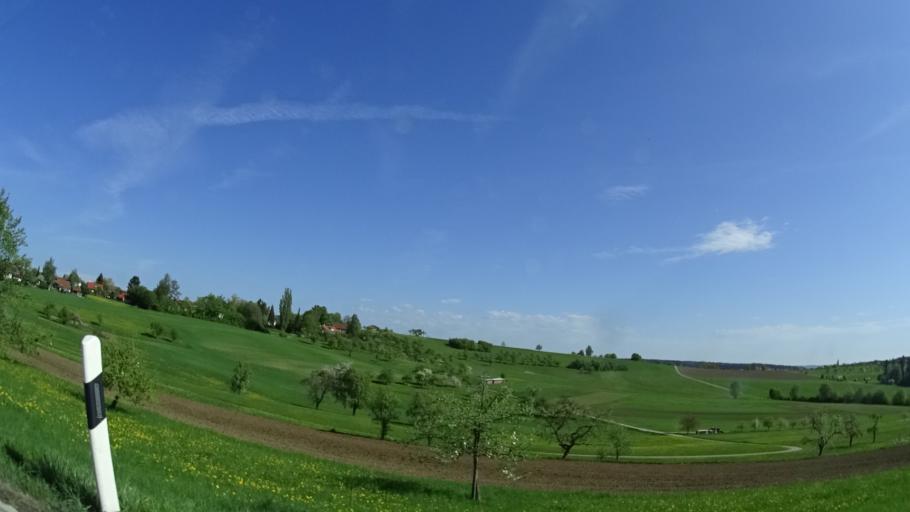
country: DE
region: Baden-Wuerttemberg
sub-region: Karlsruhe Region
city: Ebhausen
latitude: 48.6150
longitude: 8.6529
